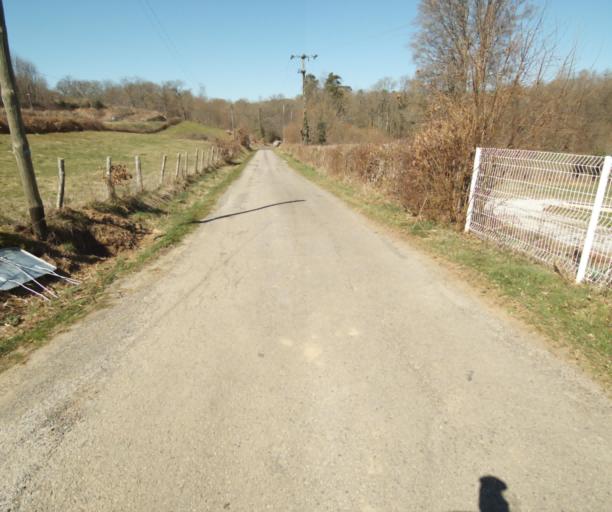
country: FR
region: Limousin
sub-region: Departement de la Correze
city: Saint-Clement
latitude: 45.3158
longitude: 1.7046
